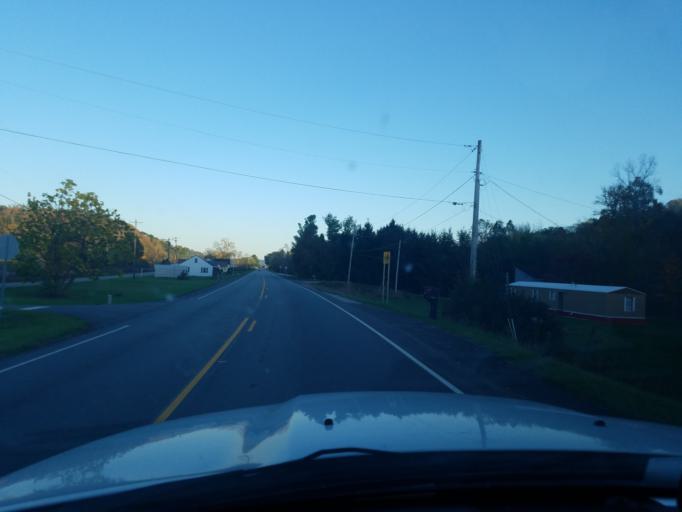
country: US
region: Indiana
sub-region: Washington County
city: New Pekin
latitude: 38.4721
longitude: -85.9624
